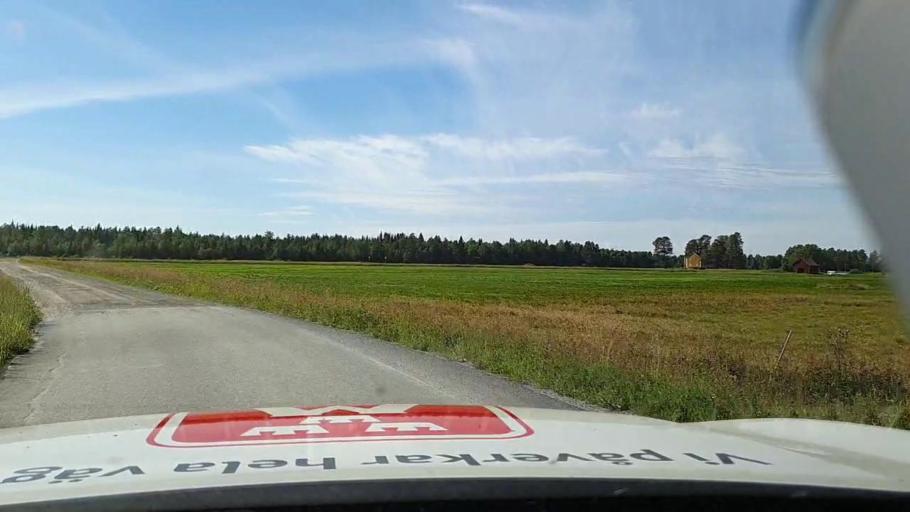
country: SE
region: Jaemtland
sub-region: Stroemsunds Kommun
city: Stroemsund
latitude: 63.6946
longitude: 15.3768
